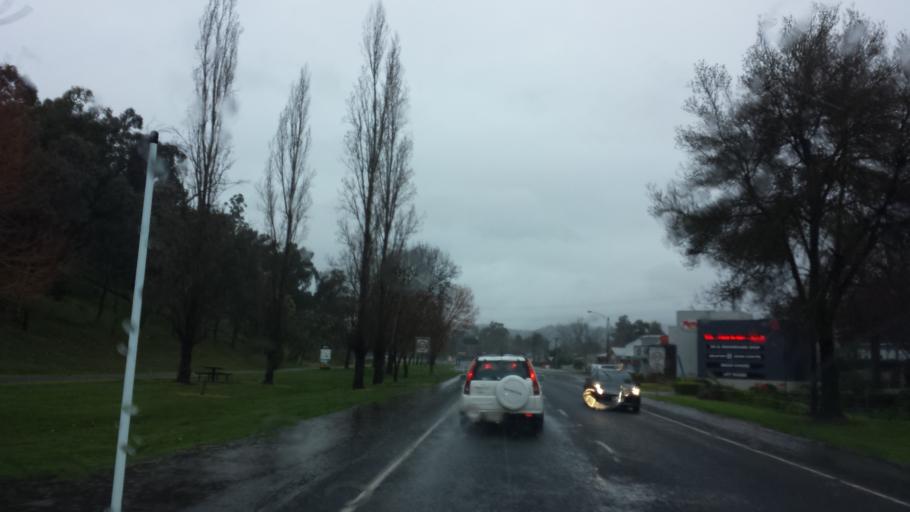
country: AU
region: Victoria
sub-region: Wangaratta
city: Wangaratta
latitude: -36.5670
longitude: 146.7301
